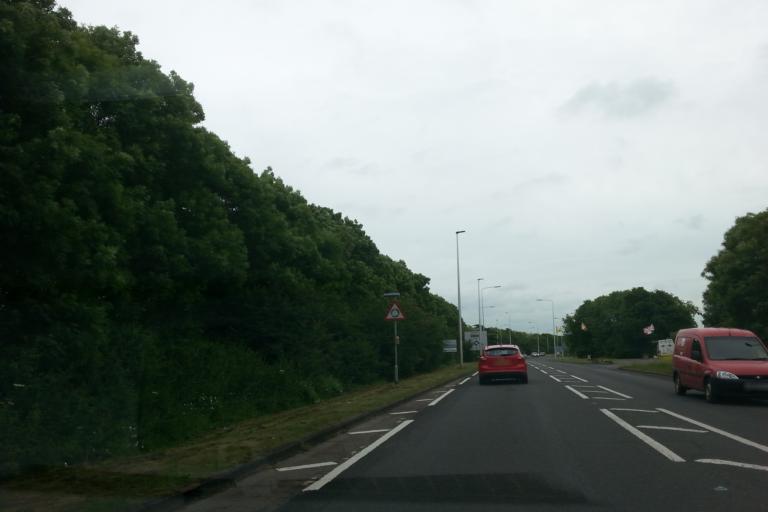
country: GB
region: England
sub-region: Peterborough
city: Castor
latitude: 52.5488
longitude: -0.3251
